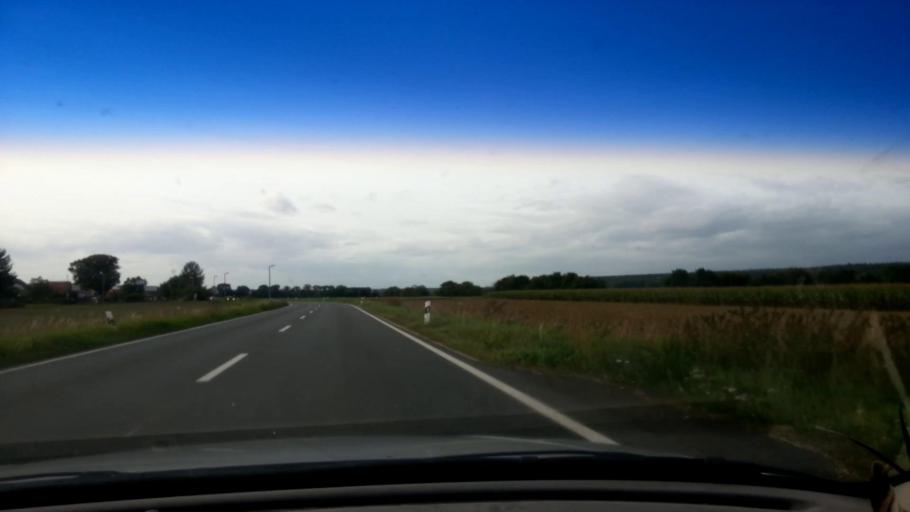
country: DE
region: Bavaria
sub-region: Upper Franconia
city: Hirschaid
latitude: 49.8290
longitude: 10.9900
